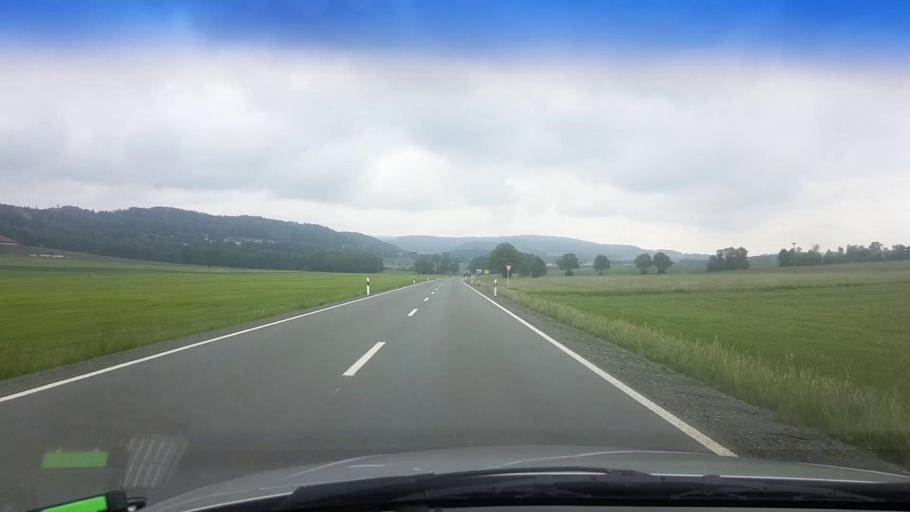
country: DE
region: Bavaria
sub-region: Upper Franconia
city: Gesees
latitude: 50.0286
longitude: 11.6555
